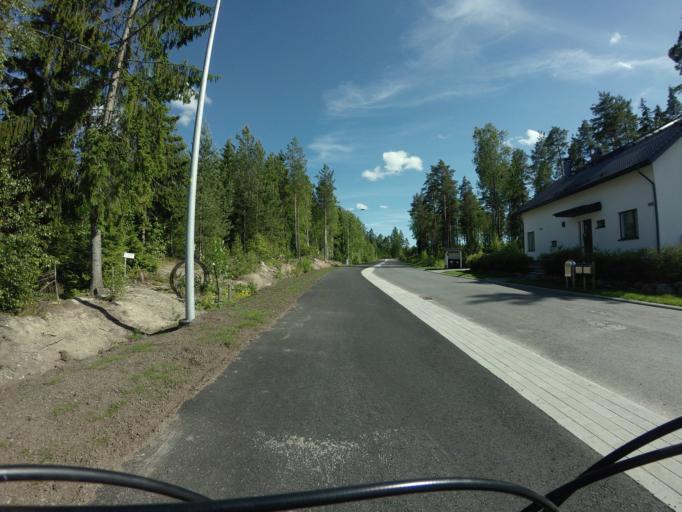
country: FI
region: Varsinais-Suomi
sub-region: Turku
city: Vahto
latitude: 60.5419
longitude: 22.3212
